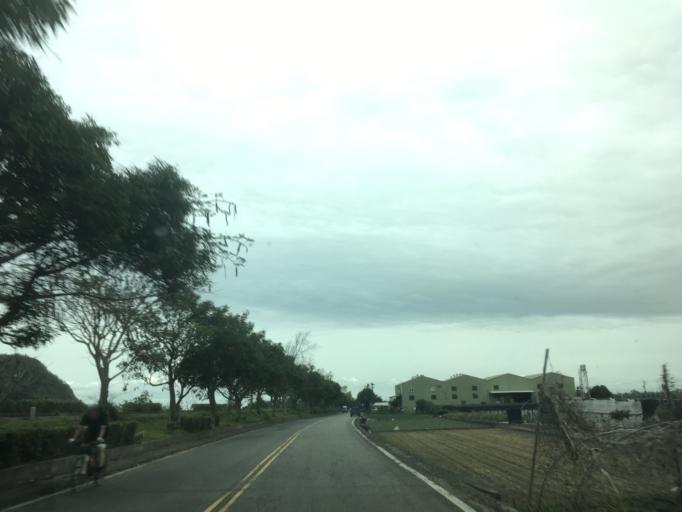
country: TW
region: Taiwan
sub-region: Taitung
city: Taitung
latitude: 22.8034
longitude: 121.1345
